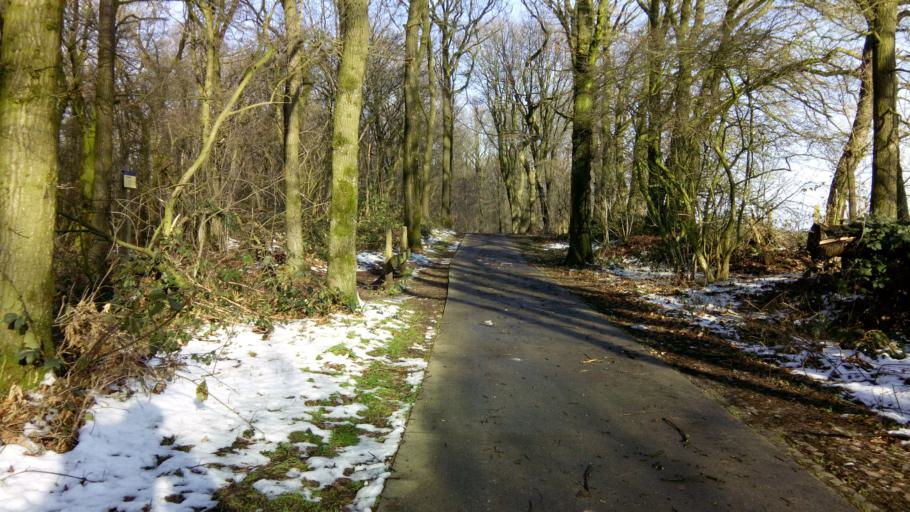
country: NL
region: North Brabant
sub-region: Gemeente Cuijk
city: Cuijk
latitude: 51.7446
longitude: 5.9078
